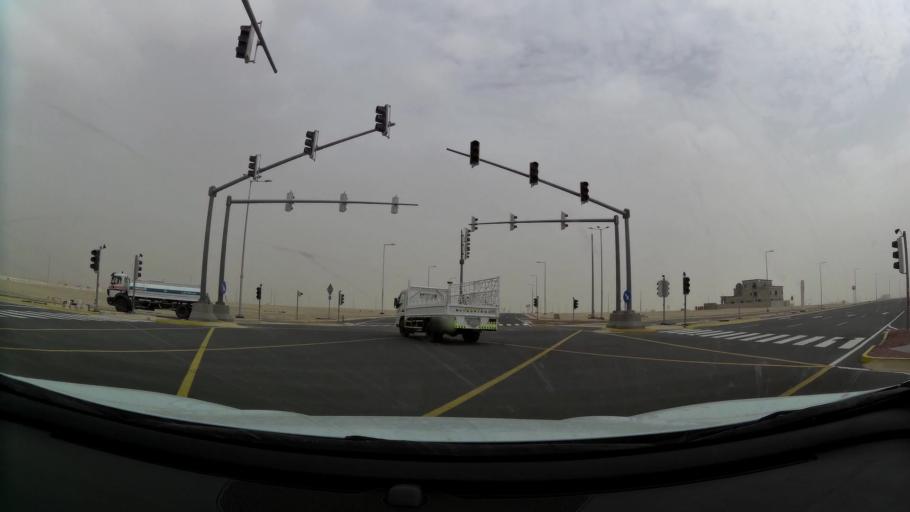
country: AE
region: Abu Dhabi
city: Abu Dhabi
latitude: 24.3706
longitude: 54.7468
